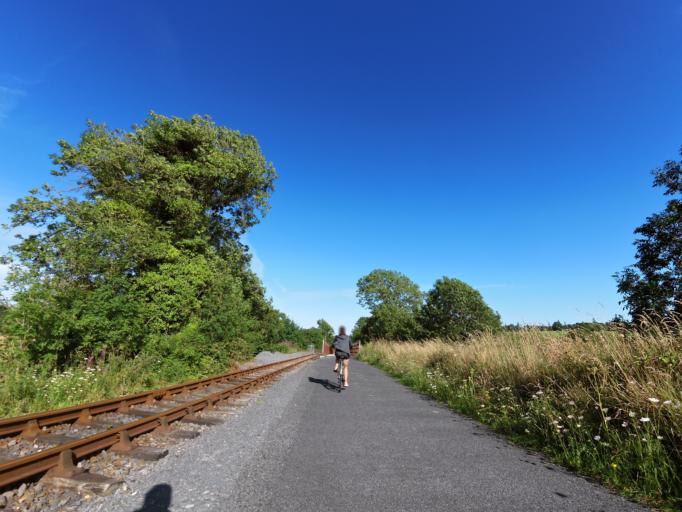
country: IE
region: Leinster
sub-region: Kilkenny
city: Mooncoin
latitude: 52.2468
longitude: -7.2333
